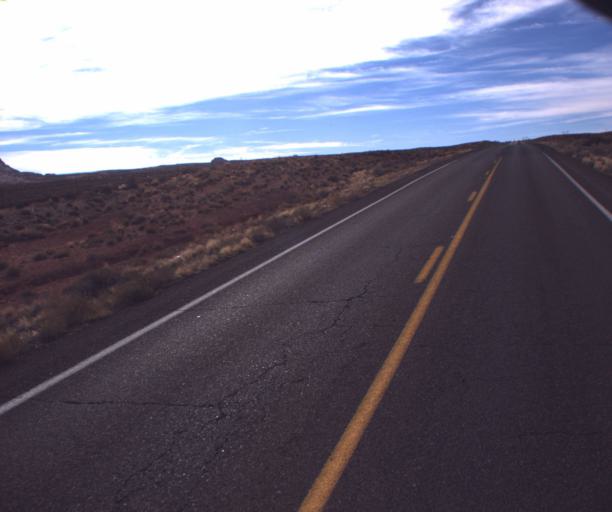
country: US
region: Arizona
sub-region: Coconino County
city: LeChee
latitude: 36.8698
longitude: -111.3413
